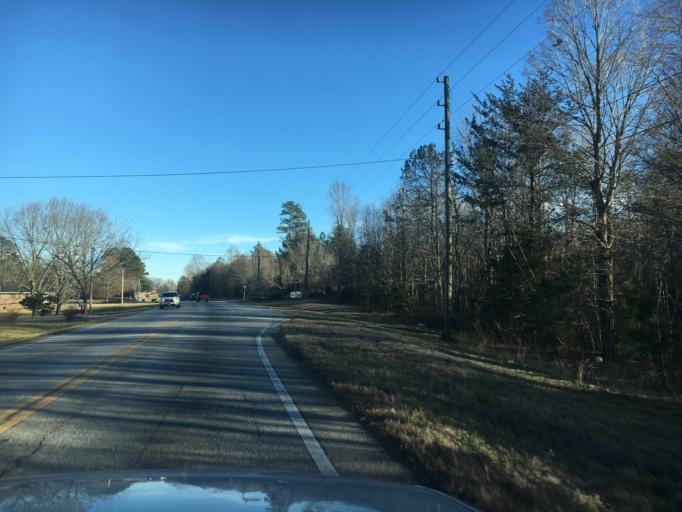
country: US
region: Georgia
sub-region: Habersham County
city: Demorest
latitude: 34.5502
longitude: -83.5638
